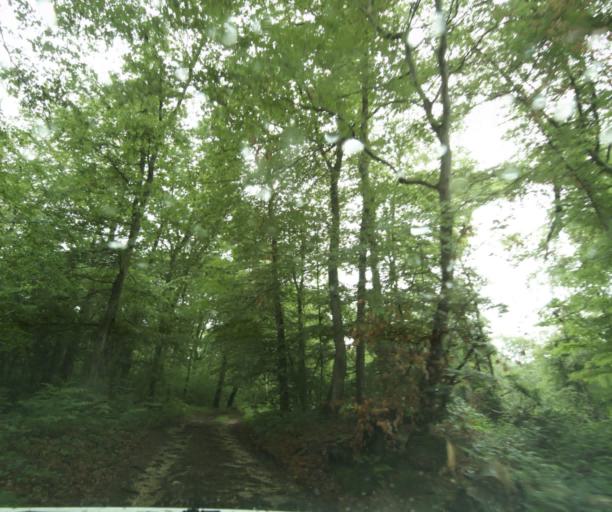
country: FR
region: Bourgogne
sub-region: Departement de Saone-et-Loire
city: Palinges
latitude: 46.5327
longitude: 4.2544
